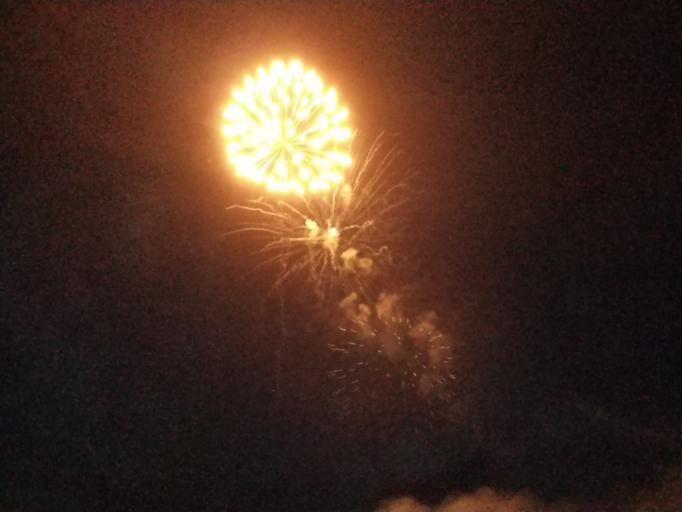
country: US
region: Colorado
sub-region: Mesa County
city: Grand Junction
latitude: 39.1084
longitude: -108.5488
